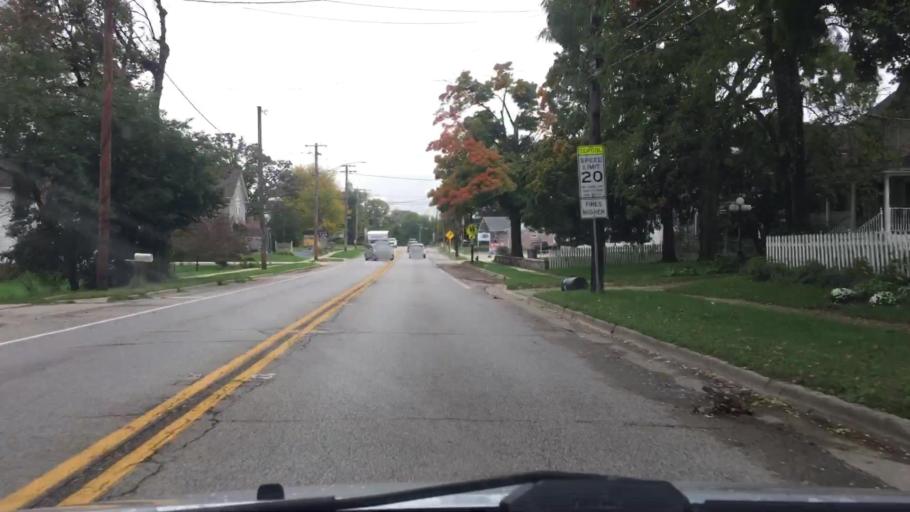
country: US
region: Illinois
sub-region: McHenry County
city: Richmond
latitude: 42.4733
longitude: -88.3063
